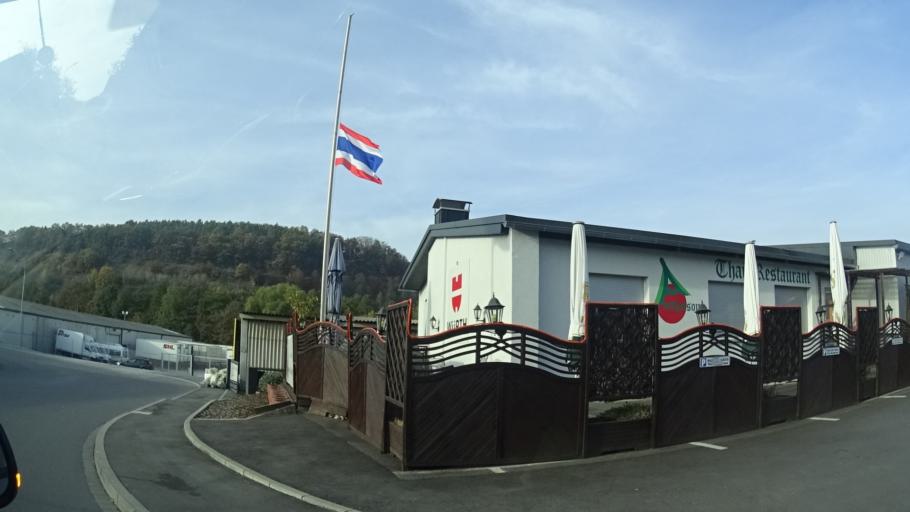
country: DE
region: Baden-Wuerttemberg
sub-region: Karlsruhe Region
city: Mosbach
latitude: 49.3448
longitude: 9.1292
